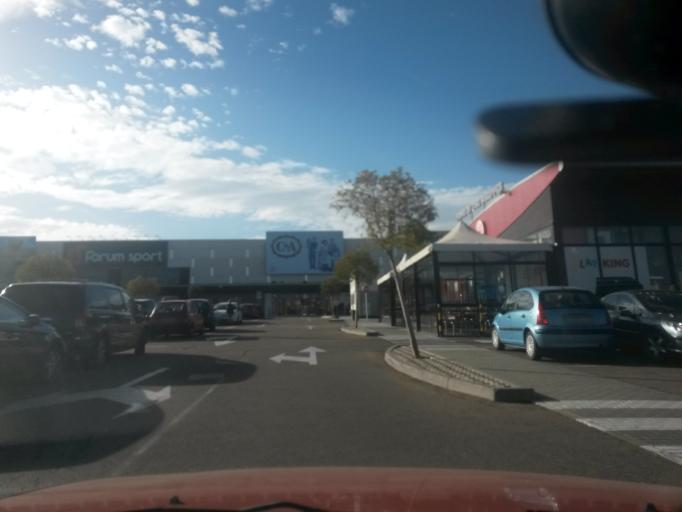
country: ES
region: Castille and Leon
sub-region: Provincia de Salamanca
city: Carbajosa de la Sagrada
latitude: 40.9493
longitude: -5.6504
